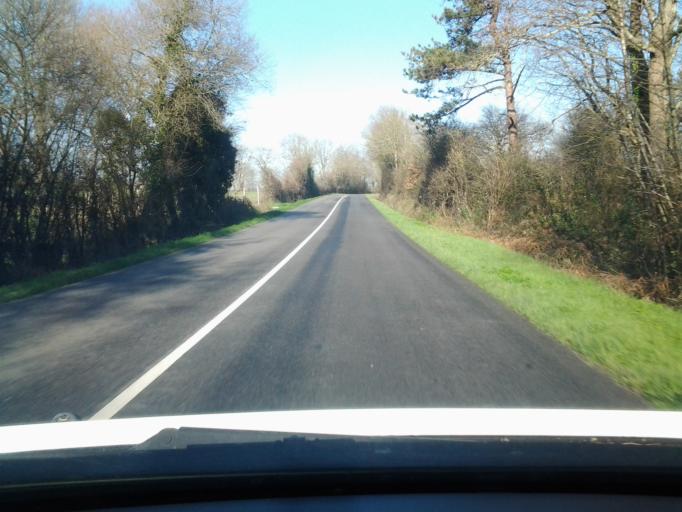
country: FR
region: Pays de la Loire
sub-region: Departement de la Vendee
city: Dompierre-sur-Yon
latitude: 46.7136
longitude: -1.4120
